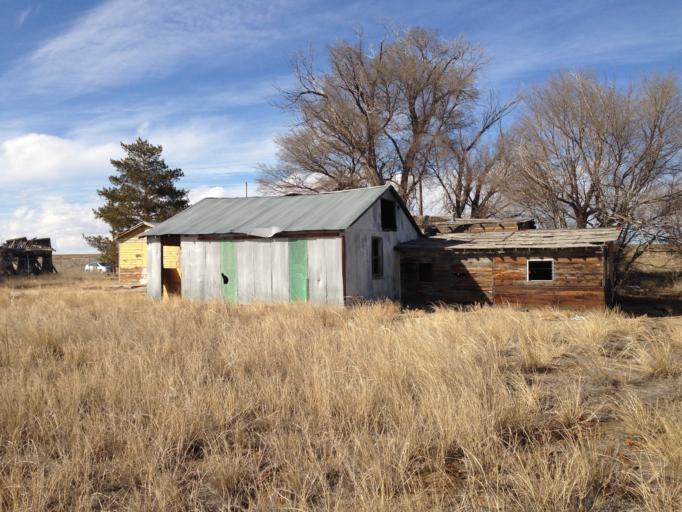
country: US
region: Colorado
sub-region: Weld County
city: Kersey
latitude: 40.2903
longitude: -104.2586
